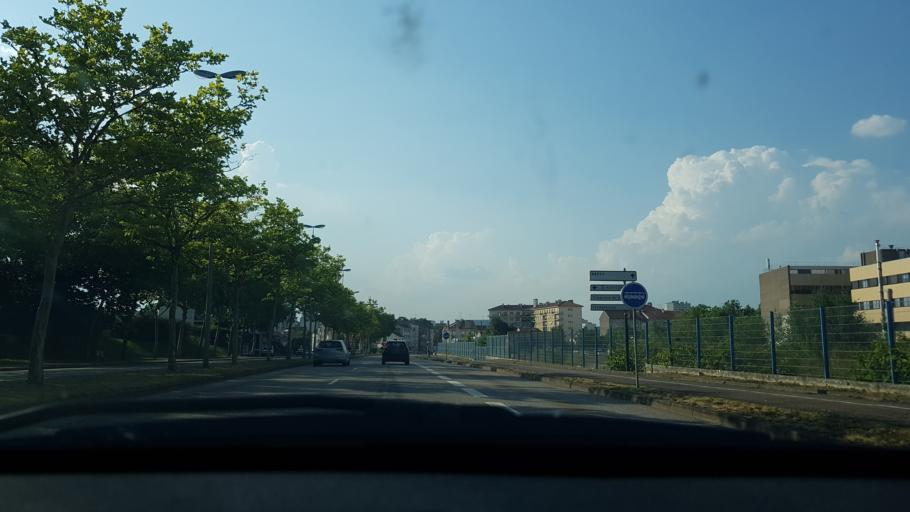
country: FR
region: Lorraine
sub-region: Departement de Meurthe-et-Moselle
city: Nancy
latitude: 48.6718
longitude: 6.1858
